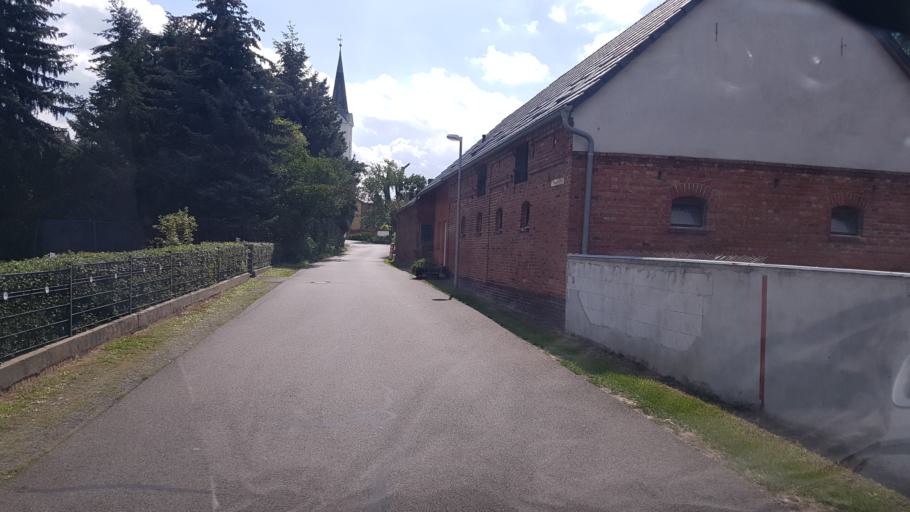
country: DE
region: Brandenburg
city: Lubbenau
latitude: 51.8638
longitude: 13.9280
